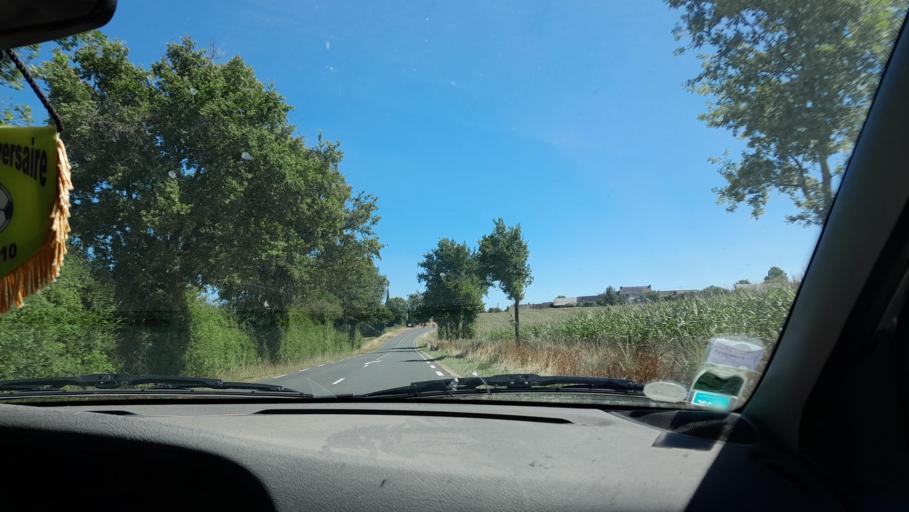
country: FR
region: Pays de la Loire
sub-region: Departement de la Loire-Atlantique
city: Saint-Mars-la-Jaille
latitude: 47.5858
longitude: -1.1943
